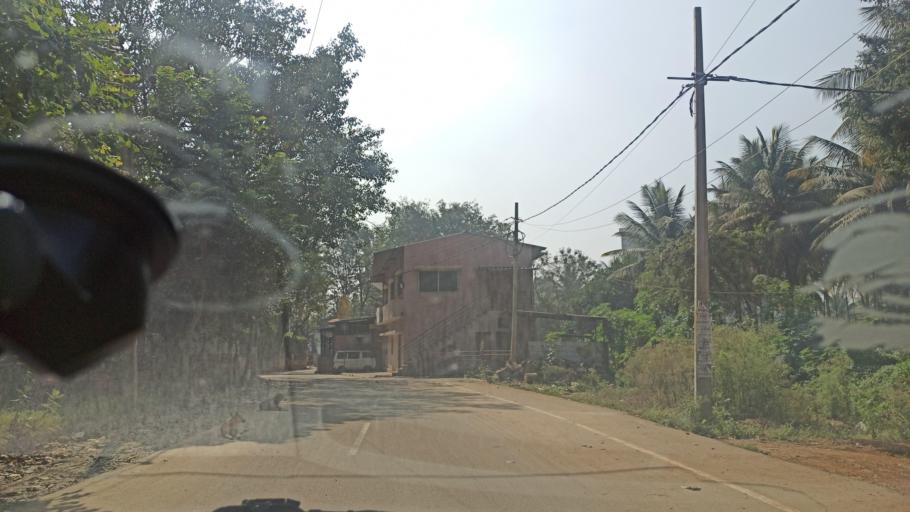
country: IN
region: Karnataka
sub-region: Bangalore Urban
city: Yelahanka
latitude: 13.0693
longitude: 77.5878
